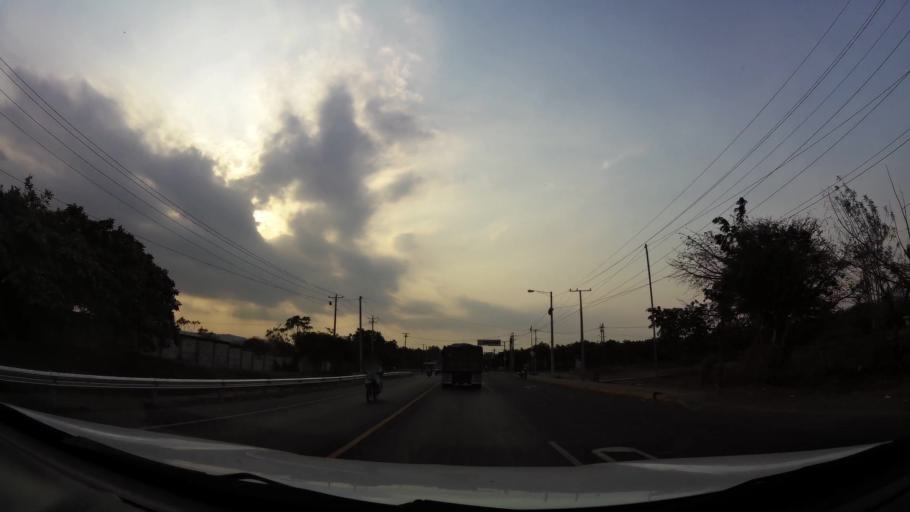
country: NI
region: Managua
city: Ciudad Sandino
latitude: 12.1805
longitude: -86.3557
